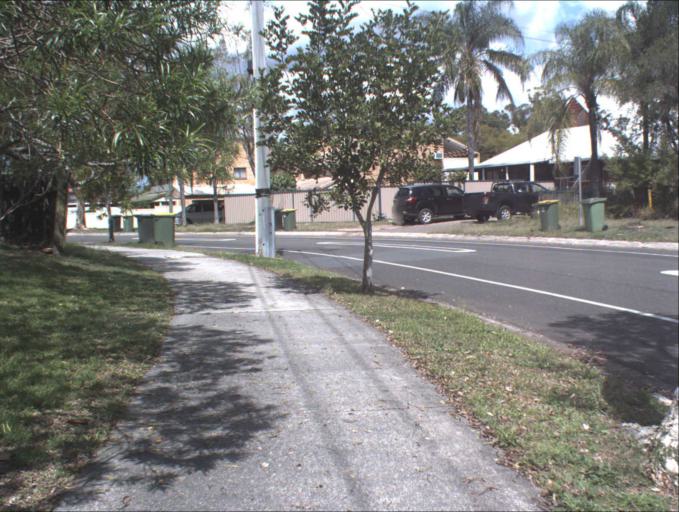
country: AU
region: Queensland
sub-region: Logan
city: Waterford West
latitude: -27.6830
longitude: 153.1464
